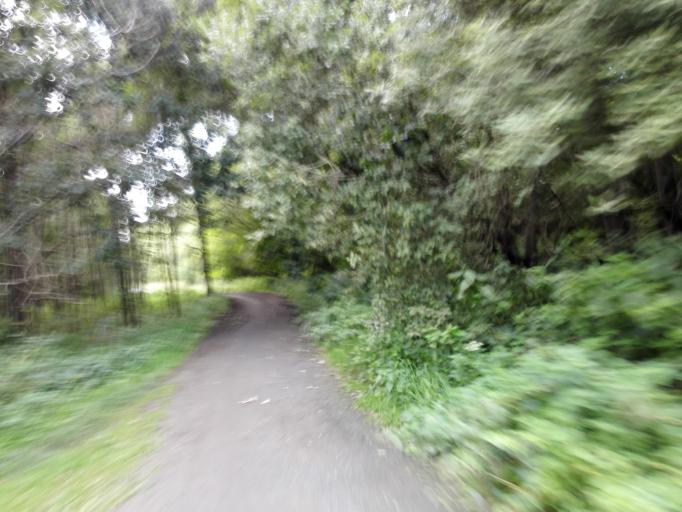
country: BE
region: Flanders
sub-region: Provincie Vlaams-Brabant
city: Oud-Heverlee
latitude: 50.8504
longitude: 4.6664
